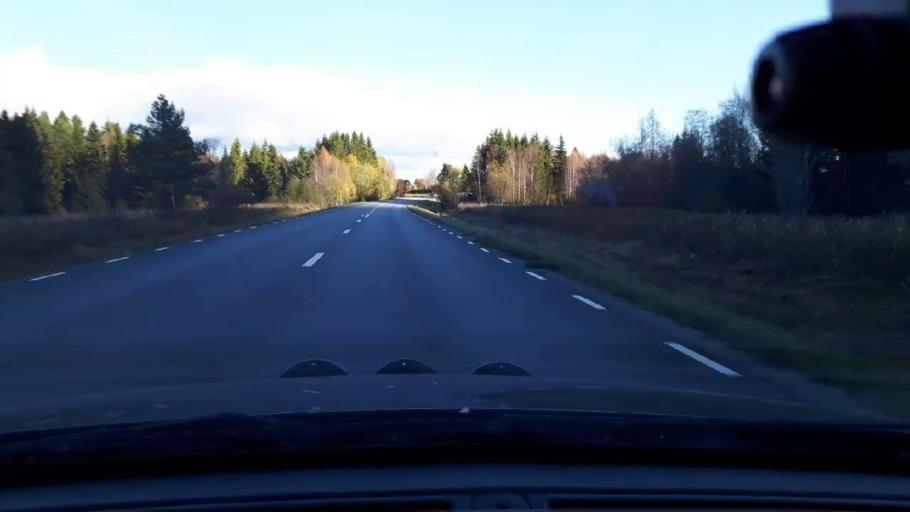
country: SE
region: Jaemtland
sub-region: Krokoms Kommun
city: Krokom
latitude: 63.0720
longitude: 14.3083
